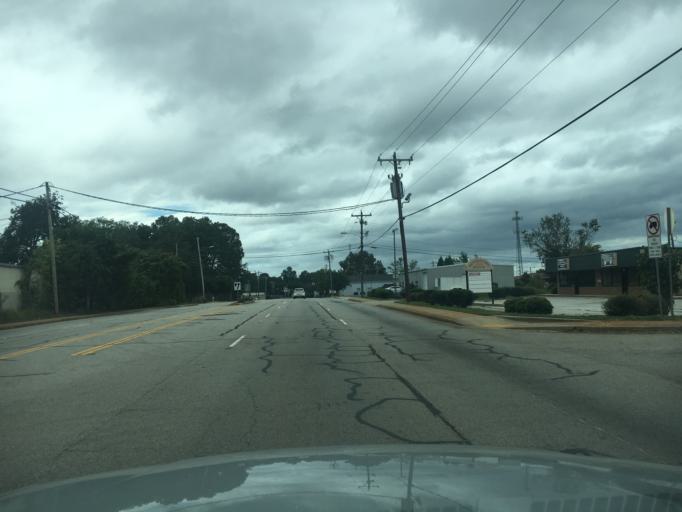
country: US
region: South Carolina
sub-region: Greenville County
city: Greenville
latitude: 34.8708
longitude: -82.4021
